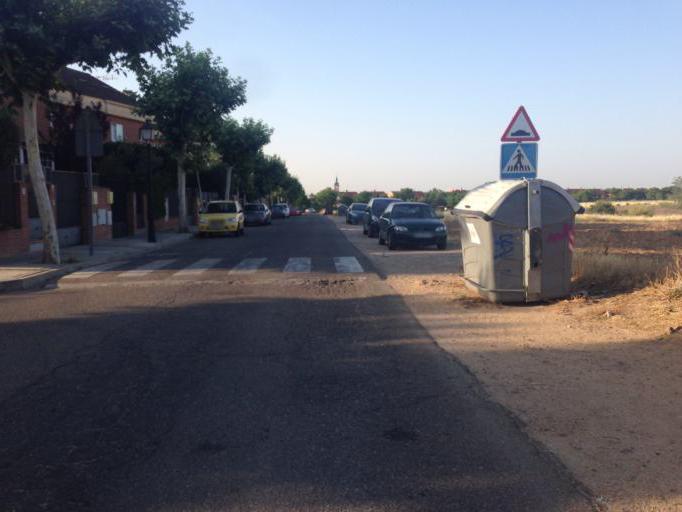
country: ES
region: Madrid
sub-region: Provincia de Madrid
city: Daganzo de Arriba
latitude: 40.5520
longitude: -3.4606
